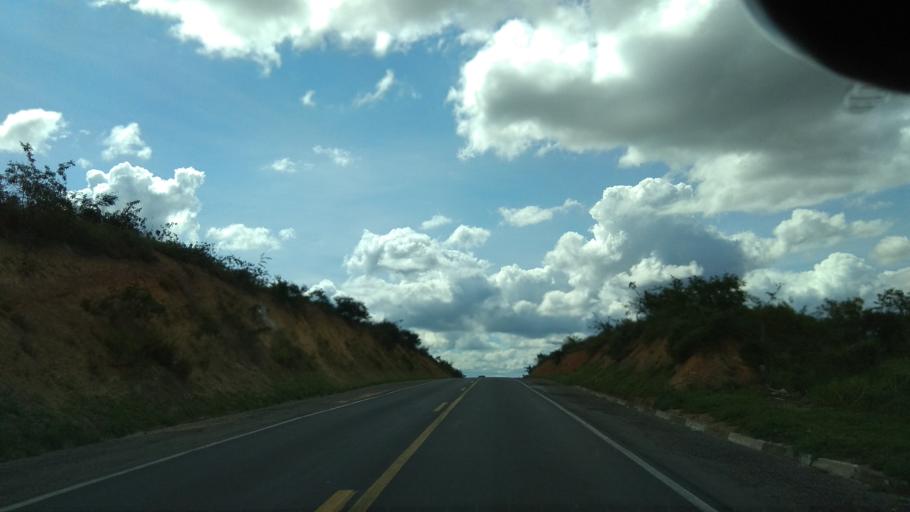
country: BR
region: Bahia
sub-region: Jaguaquara
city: Jaguaquara
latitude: -13.4555
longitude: -40.0324
